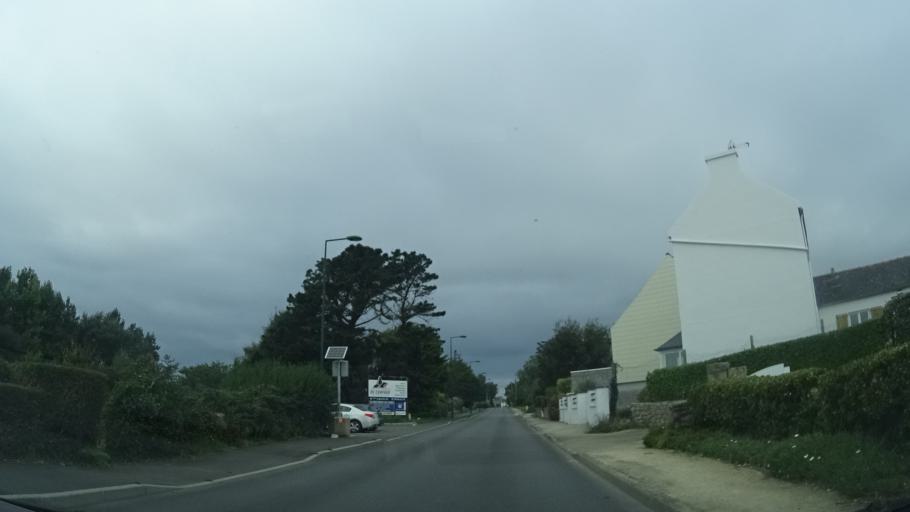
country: FR
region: Brittany
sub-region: Departement du Finistere
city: Lampaul-Plouarzel
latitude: 48.4741
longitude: -4.7559
